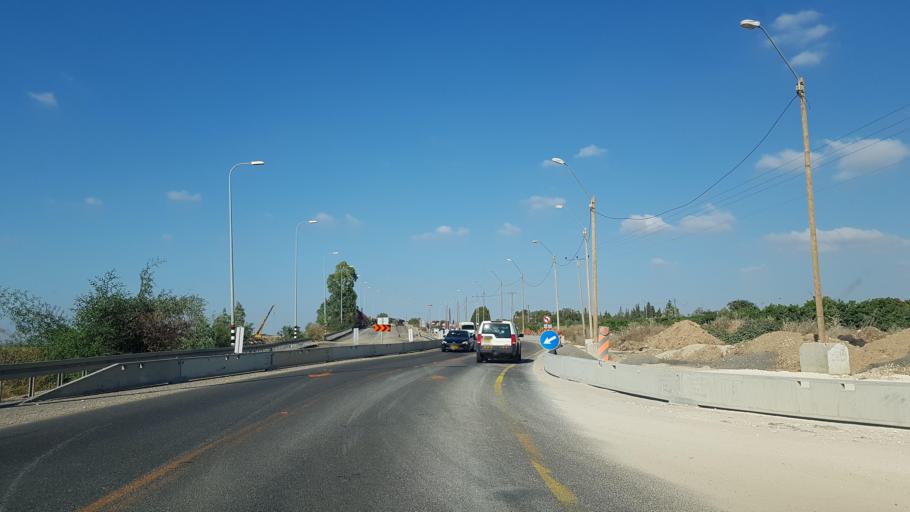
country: PS
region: West Bank
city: Tulkarm
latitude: 32.3335
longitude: 35.0060
